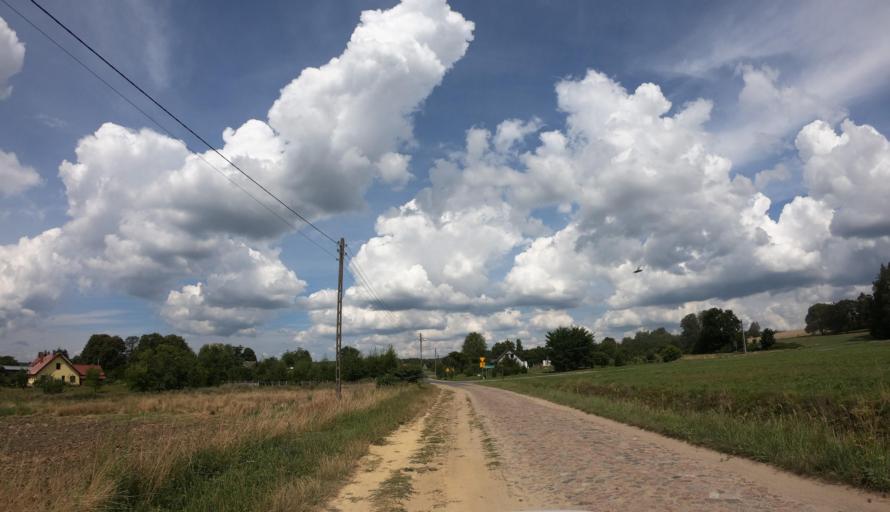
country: PL
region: West Pomeranian Voivodeship
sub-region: Powiat stargardzki
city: Kobylanka
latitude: 53.3210
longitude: 14.8254
